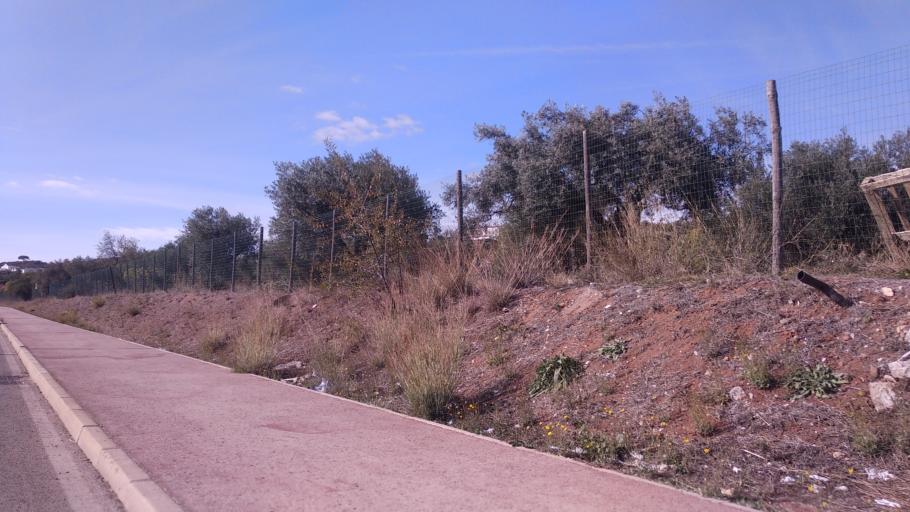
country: PT
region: Faro
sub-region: Sao Bras de Alportel
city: Sao Bras de Alportel
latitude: 37.1566
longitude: -7.8836
